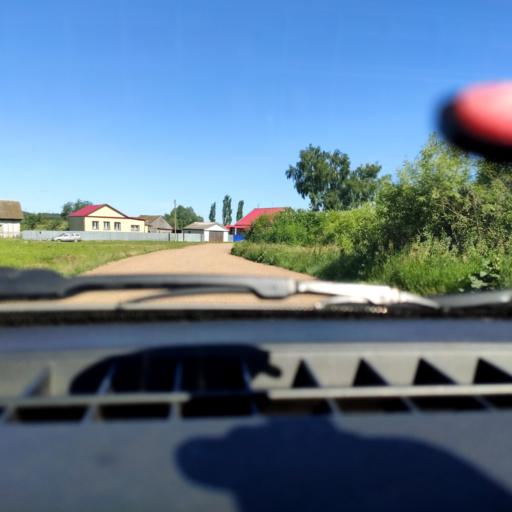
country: RU
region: Bashkortostan
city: Iglino
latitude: 54.8990
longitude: 56.4905
